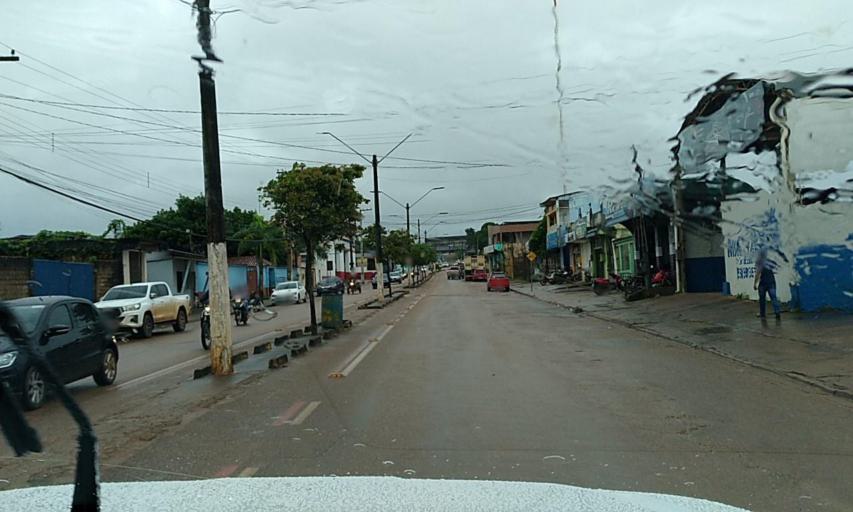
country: BR
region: Para
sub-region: Altamira
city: Altamira
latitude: -3.2115
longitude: -52.2253
